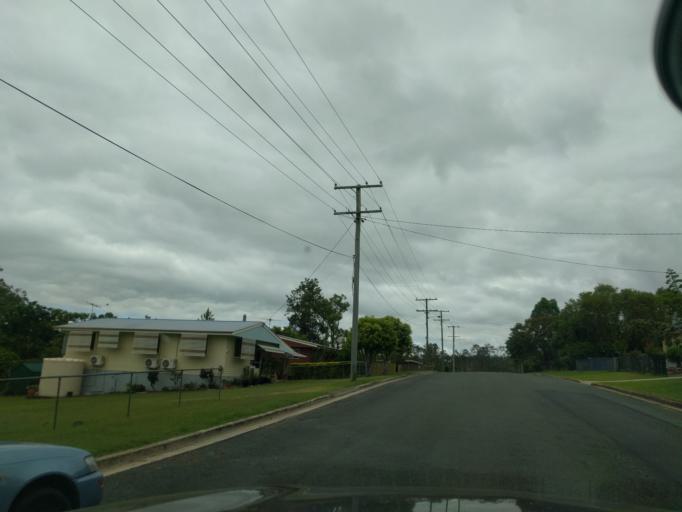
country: AU
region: Queensland
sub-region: Logan
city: Cedar Vale
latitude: -27.9874
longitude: 153.0094
